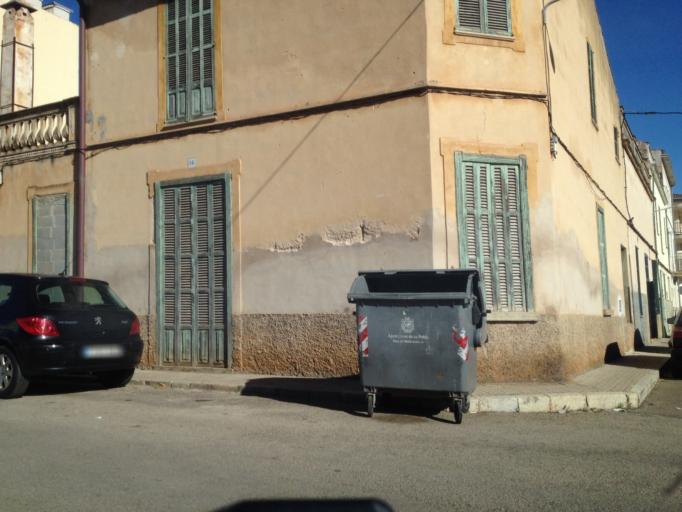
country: ES
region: Balearic Islands
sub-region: Illes Balears
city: sa Pobla
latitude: 39.7705
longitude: 3.0287
